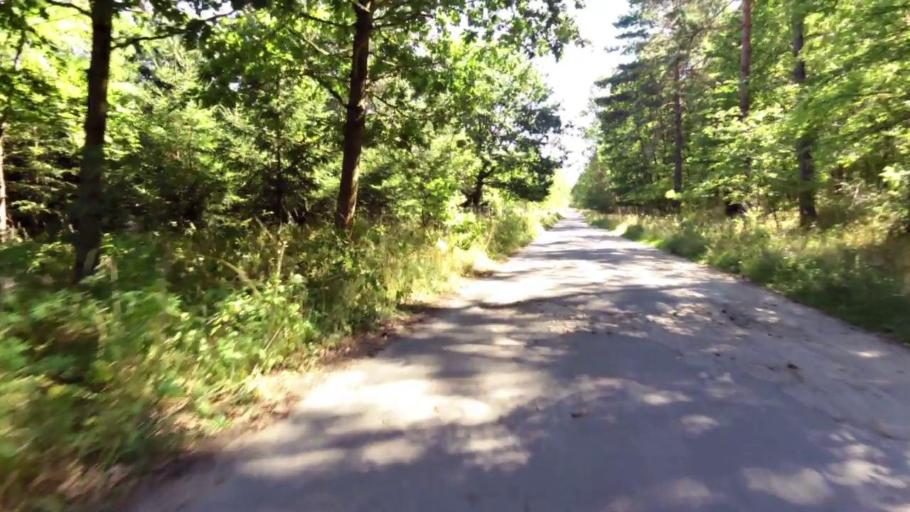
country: PL
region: West Pomeranian Voivodeship
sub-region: Powiat szczecinecki
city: Borne Sulinowo
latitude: 53.5944
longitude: 16.6422
